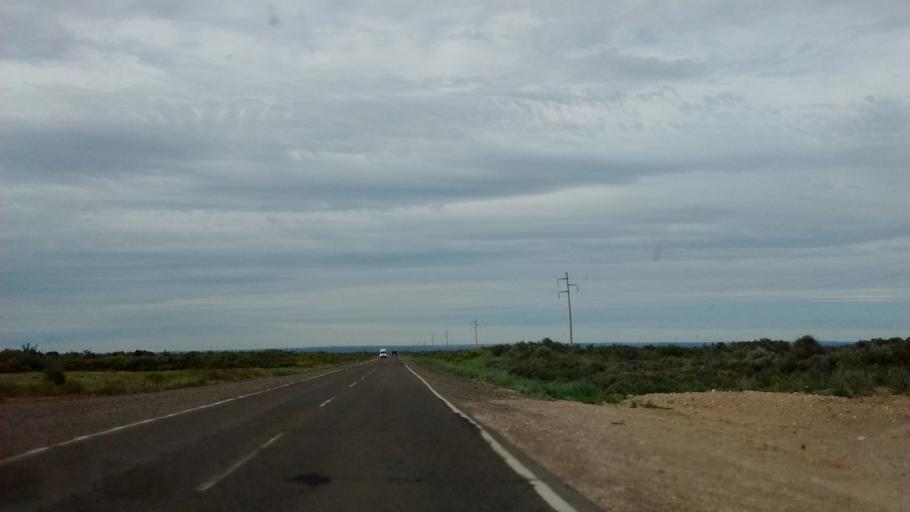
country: AR
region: Rio Negro
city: Catriel
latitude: -37.9412
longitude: -67.8853
